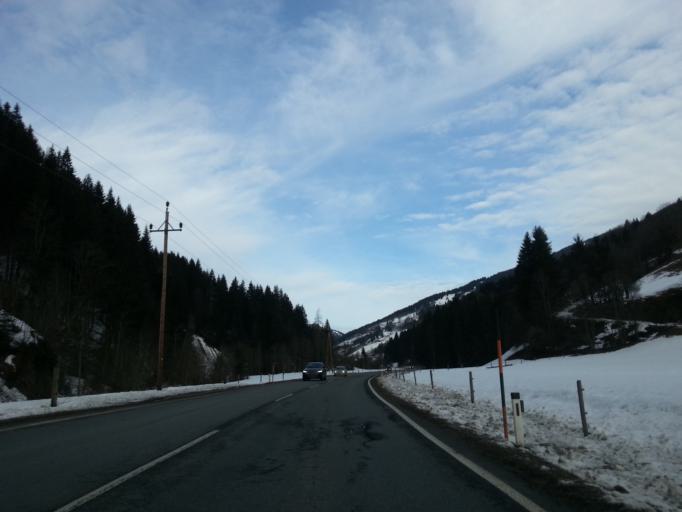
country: AT
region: Salzburg
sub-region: Politischer Bezirk Zell am See
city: Viehhofen
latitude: 47.3691
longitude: 12.6981
